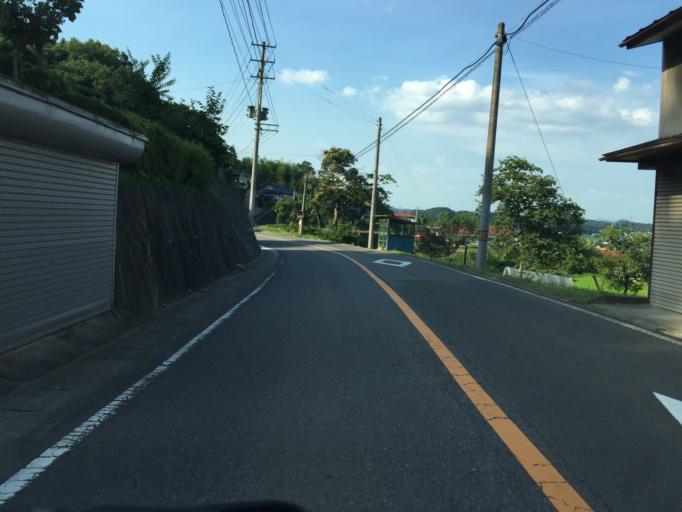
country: JP
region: Fukushima
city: Nihommatsu
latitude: 37.5542
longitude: 140.4109
